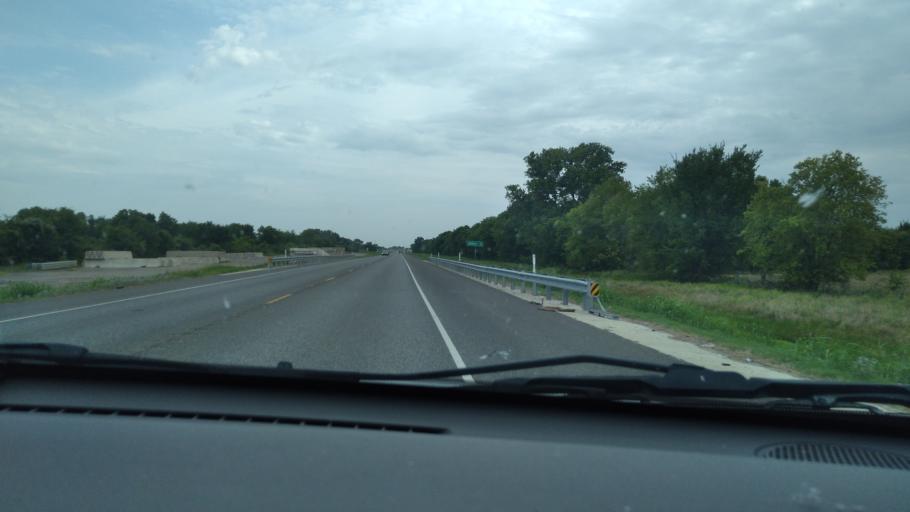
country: US
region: Texas
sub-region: McLennan County
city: Bellmead
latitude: 31.5623
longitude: -97.0677
